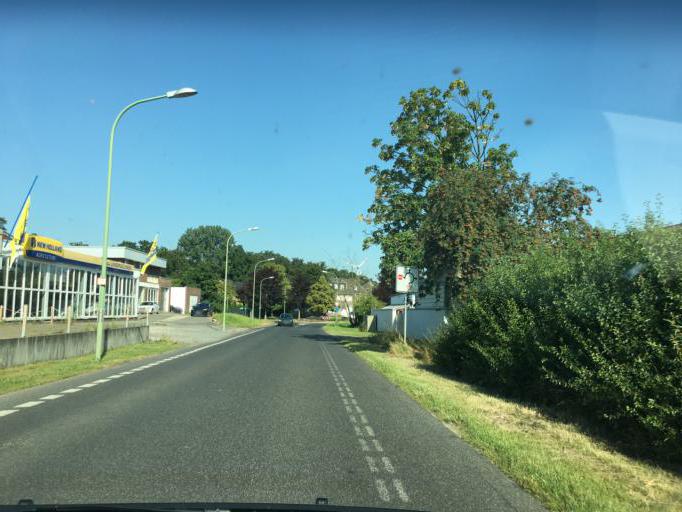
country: DE
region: North Rhine-Westphalia
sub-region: Regierungsbezirk Koln
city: Dueren
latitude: 50.8210
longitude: 6.4236
